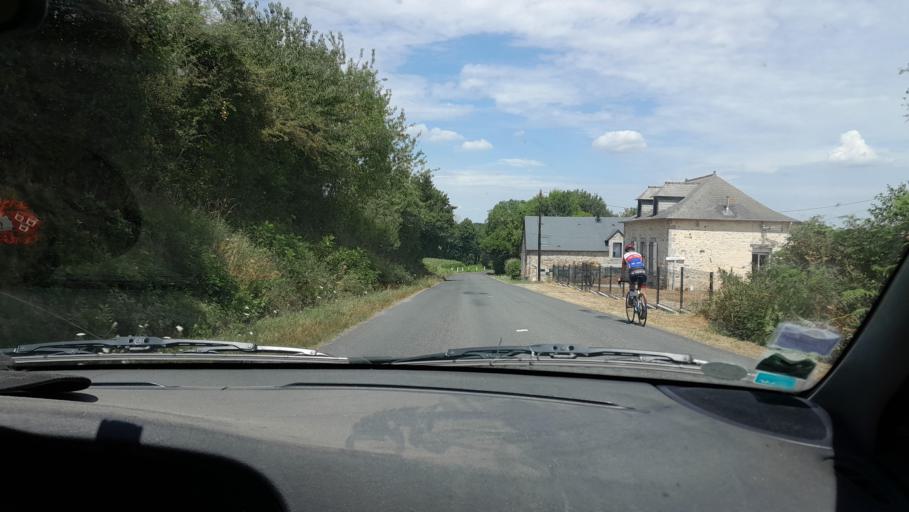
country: FR
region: Pays de la Loire
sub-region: Departement de la Mayenne
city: Saint-Pierre-la-Cour
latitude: 48.0852
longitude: -1.0177
